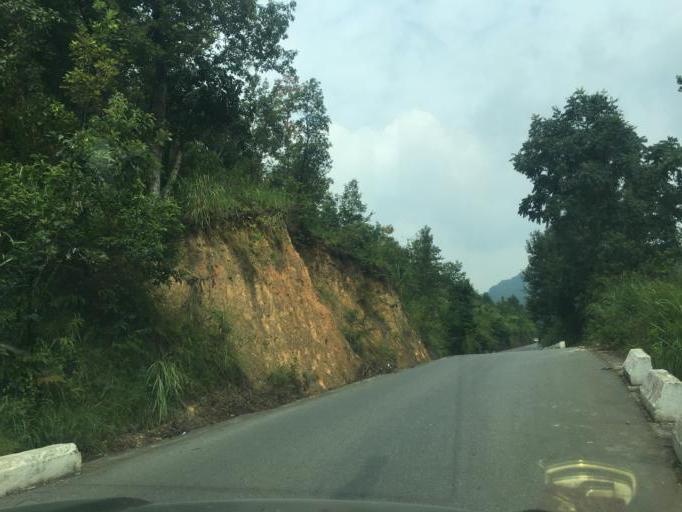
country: CN
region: Guangxi Zhuangzu Zizhiqu
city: Tongle
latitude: 25.3316
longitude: 106.0023
